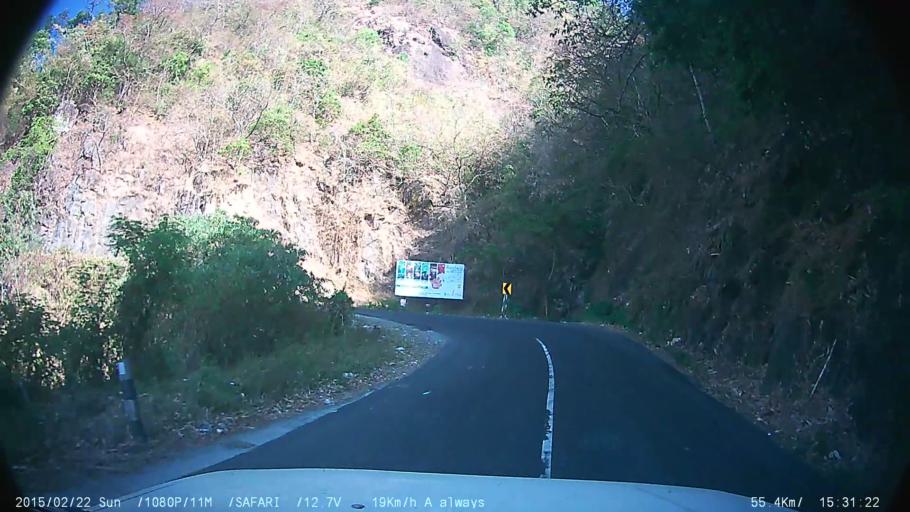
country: IN
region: Kerala
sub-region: Kottayam
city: Erattupetta
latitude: 9.5576
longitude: 76.9572
